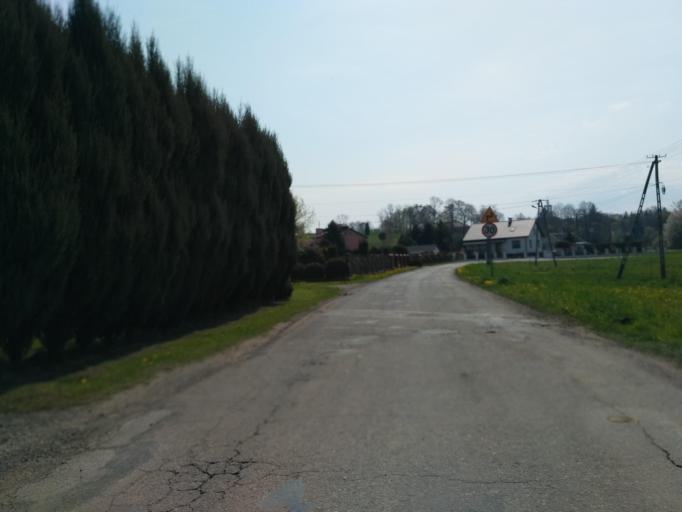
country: PL
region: Subcarpathian Voivodeship
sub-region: Powiat krosnienski
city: Chorkowka
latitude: 49.6357
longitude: 21.7289
